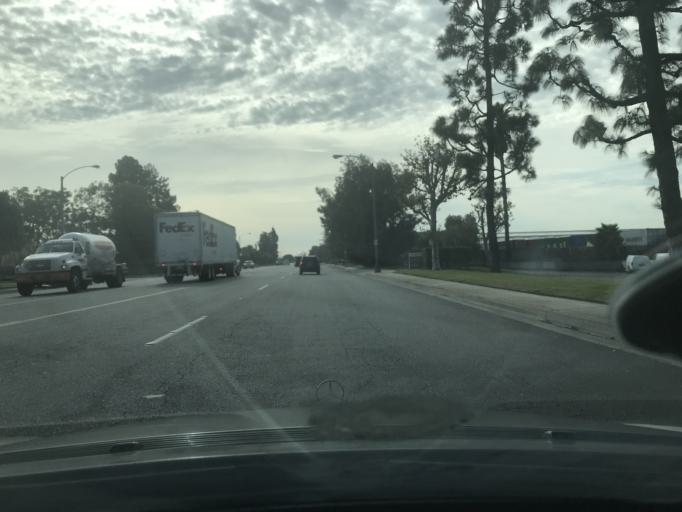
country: US
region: California
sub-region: Los Angeles County
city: Santa Fe Springs
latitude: 33.9535
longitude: -118.0723
